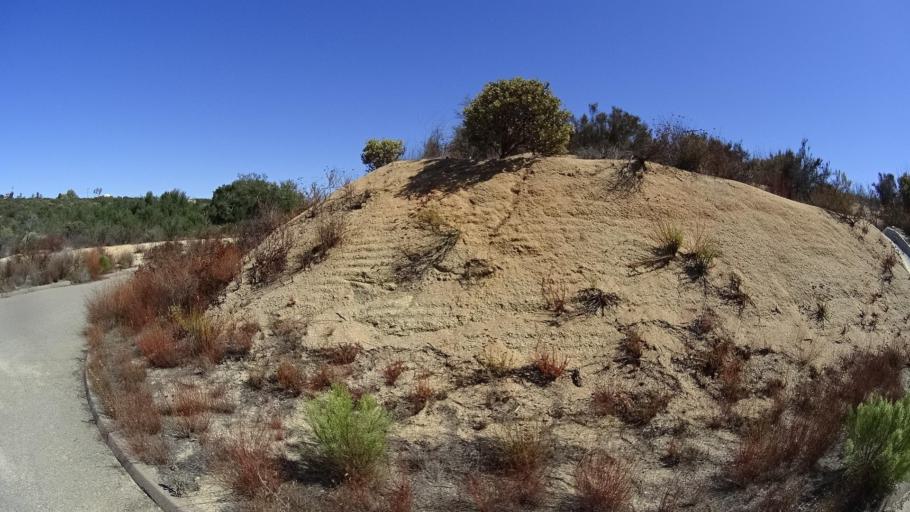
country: US
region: California
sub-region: San Diego County
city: Alpine
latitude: 32.7592
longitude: -116.7717
